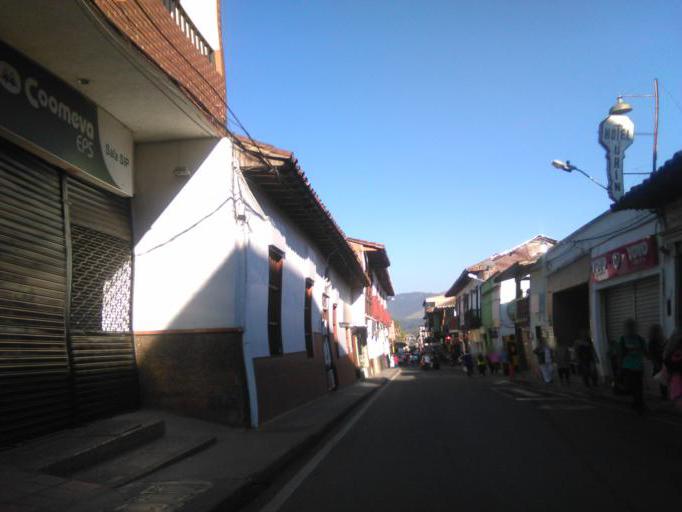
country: CO
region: Antioquia
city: La Ceja
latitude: 6.0306
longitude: -75.4328
